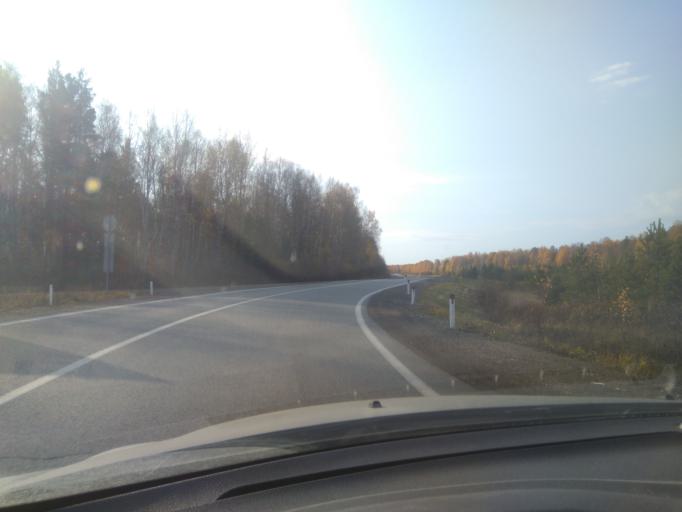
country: RU
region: Sverdlovsk
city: Atig
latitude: 56.7333
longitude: 59.4315
